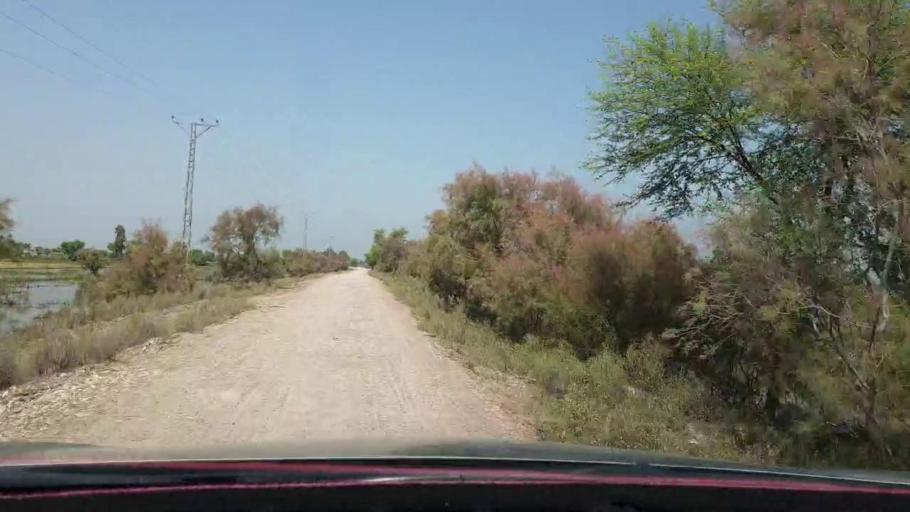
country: PK
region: Sindh
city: Warah
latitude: 27.4103
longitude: 67.6984
